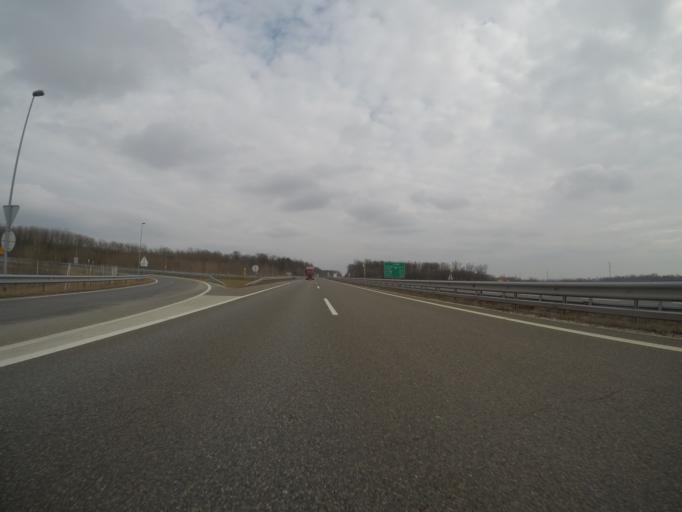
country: SI
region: Beltinci
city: Gancani
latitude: 46.6386
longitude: 16.2614
